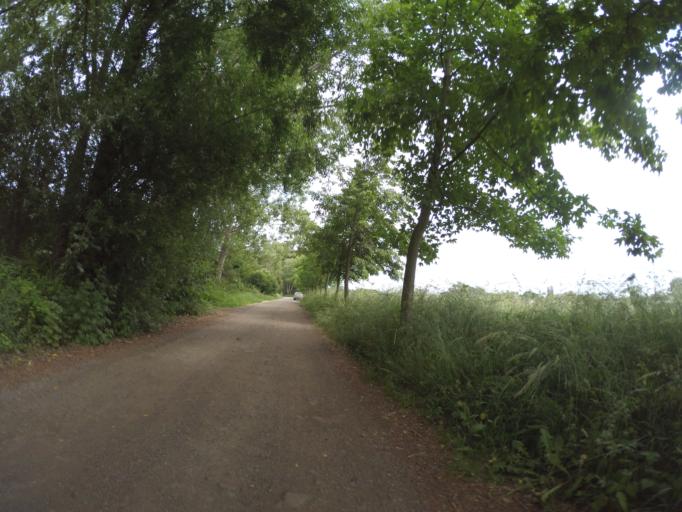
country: CZ
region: Central Bohemia
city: Celakovice
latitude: 50.1718
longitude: 14.7599
